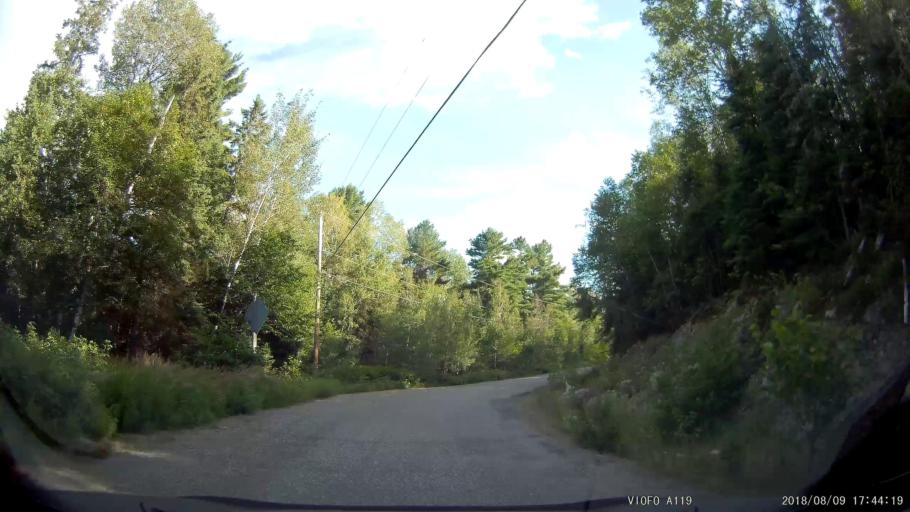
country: CA
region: Ontario
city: Rayside-Balfour
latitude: 46.6068
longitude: -81.5330
